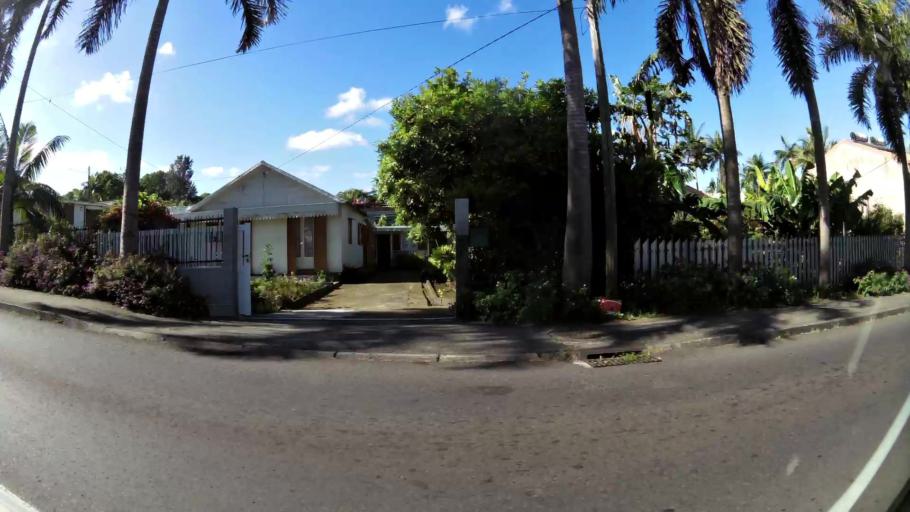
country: RE
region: Reunion
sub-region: Reunion
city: Le Tampon
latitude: -21.2672
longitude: 55.5244
